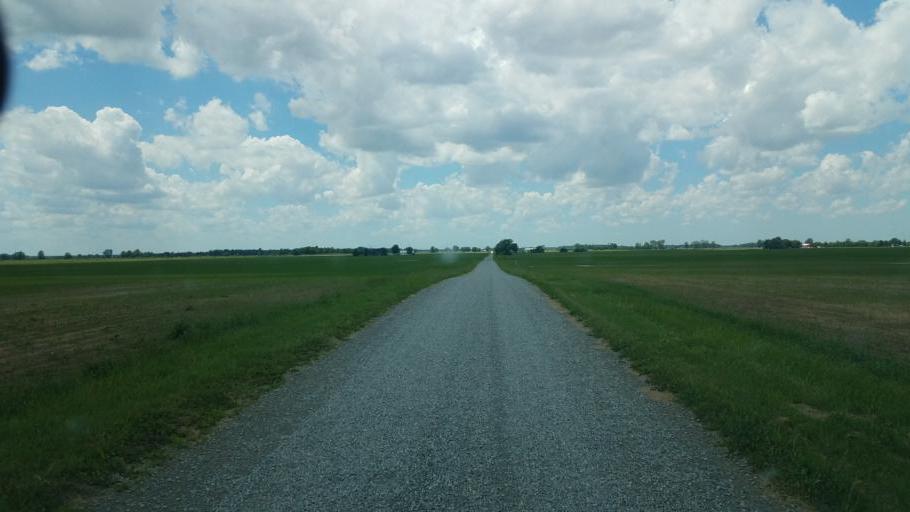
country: US
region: Ohio
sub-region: Wyandot County
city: Upper Sandusky
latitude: 40.7600
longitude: -83.2460
